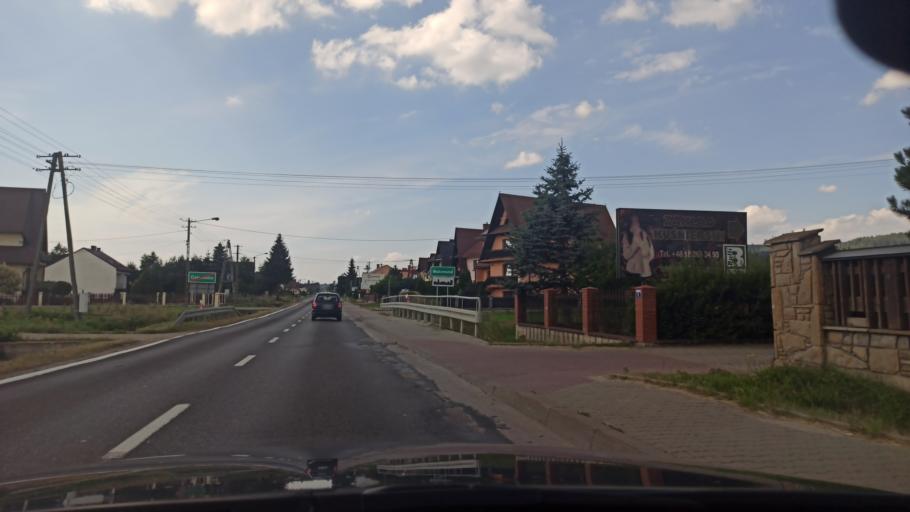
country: PL
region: Lesser Poland Voivodeship
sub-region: Powiat nowotarski
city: Ostrowsko
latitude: 49.4777
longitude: 20.0912
